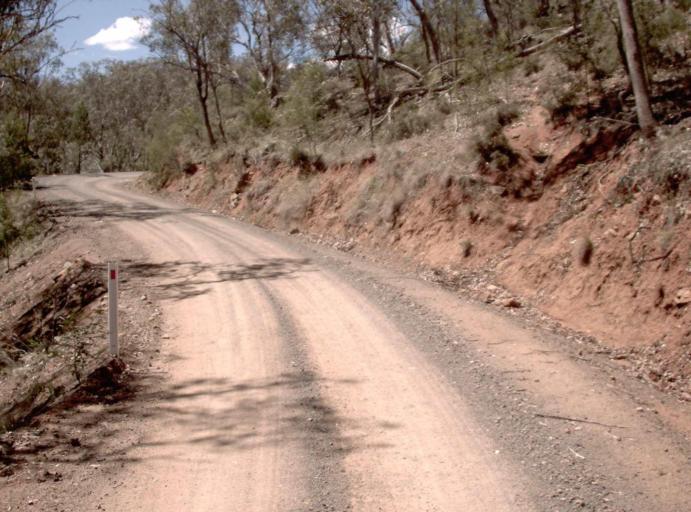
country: AU
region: New South Wales
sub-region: Snowy River
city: Jindabyne
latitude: -37.0561
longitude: 148.5339
